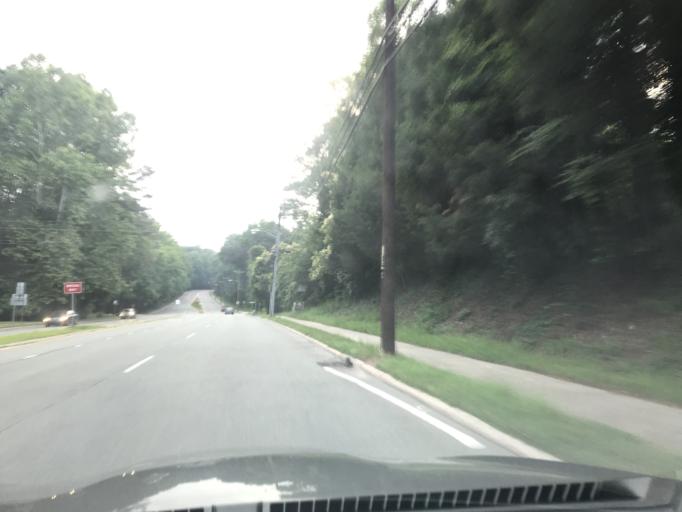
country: US
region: North Carolina
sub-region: Orange County
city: Chapel Hill
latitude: 35.9096
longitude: -79.0305
